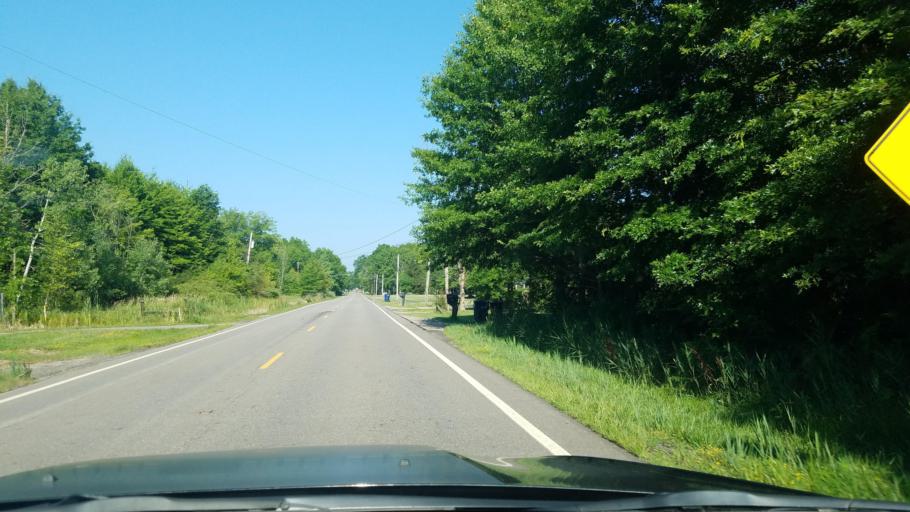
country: US
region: Ohio
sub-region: Trumbull County
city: Champion Heights
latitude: 41.3084
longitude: -80.8759
